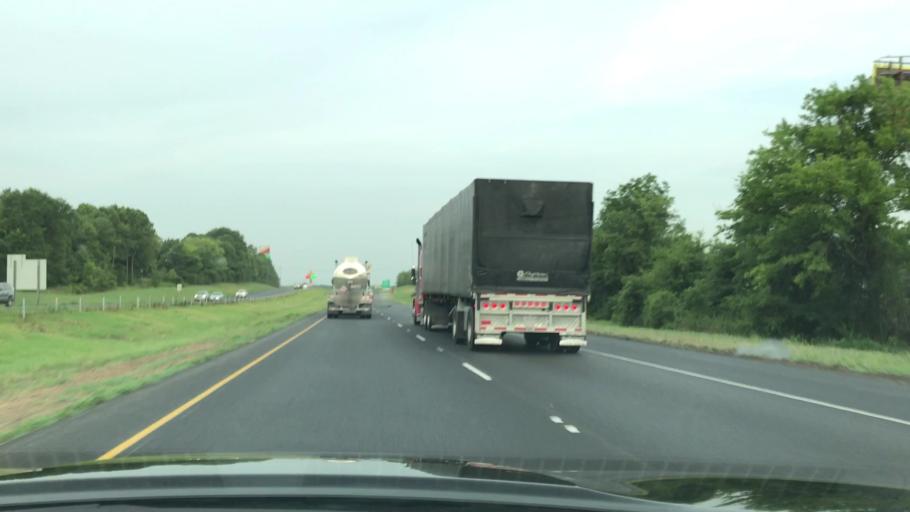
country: US
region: Louisiana
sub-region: Caddo Parish
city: Greenwood
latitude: 32.4461
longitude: -93.9709
